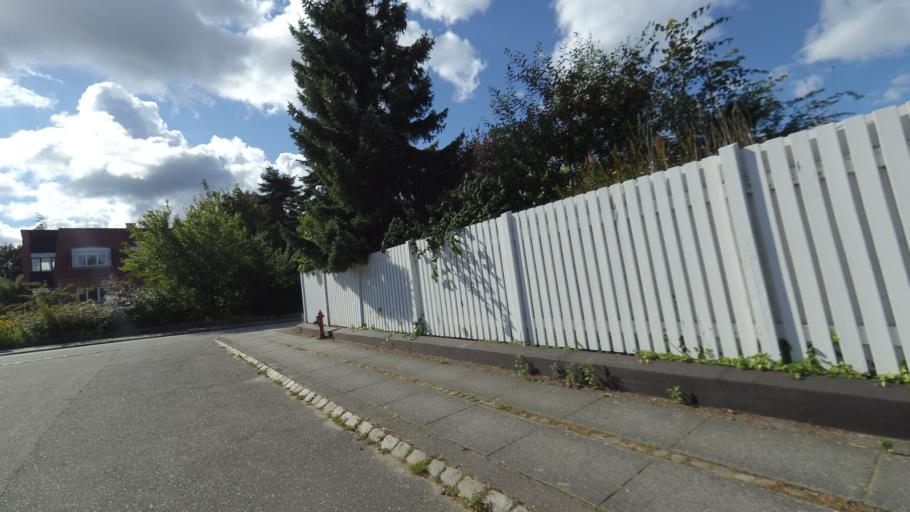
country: DK
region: Central Jutland
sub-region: Arhus Kommune
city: Arhus
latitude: 56.1160
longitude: 10.2024
